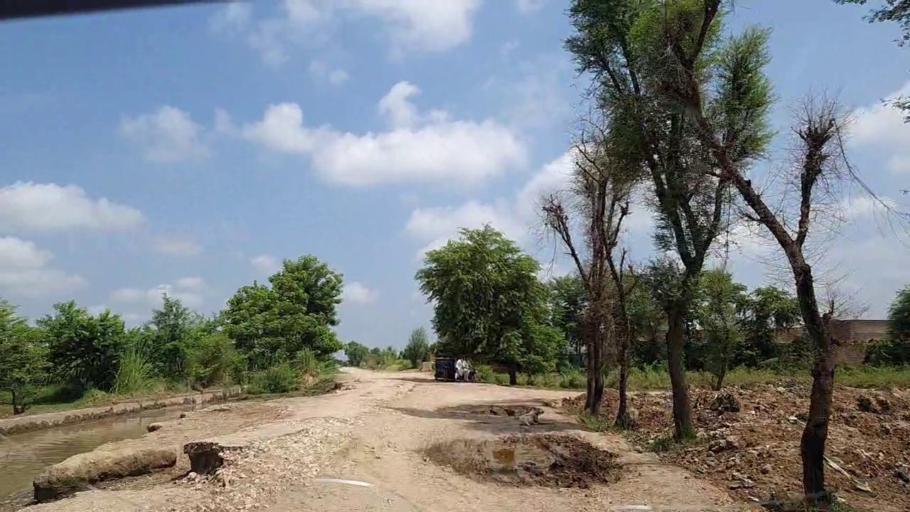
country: PK
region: Sindh
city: Tharu Shah
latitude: 26.8994
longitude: 68.0396
